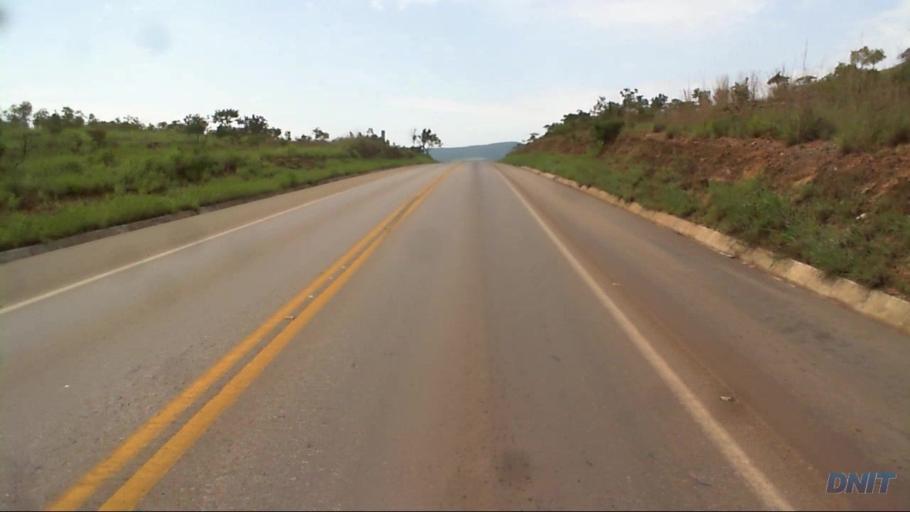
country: BR
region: Goias
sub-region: Barro Alto
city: Barro Alto
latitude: -15.1706
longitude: -48.7963
